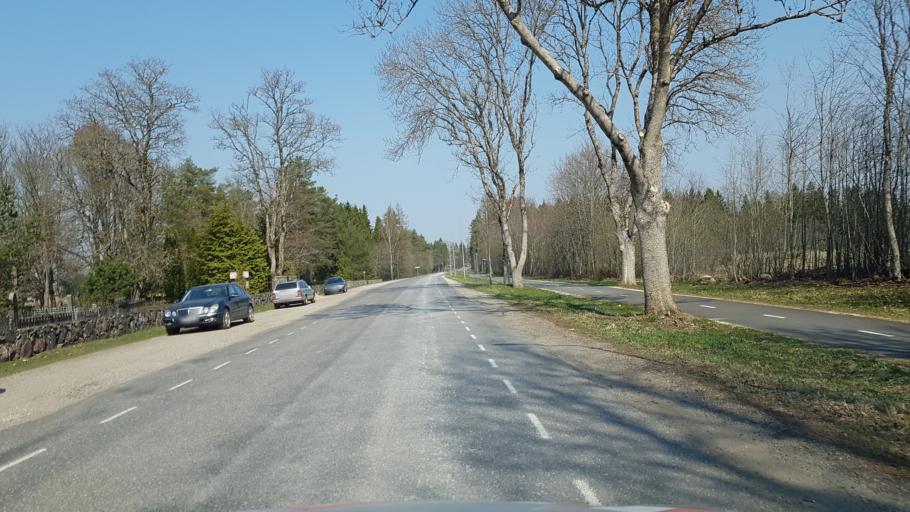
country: EE
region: Raplamaa
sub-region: Kohila vald
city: Kohila
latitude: 59.1660
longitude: 24.6519
